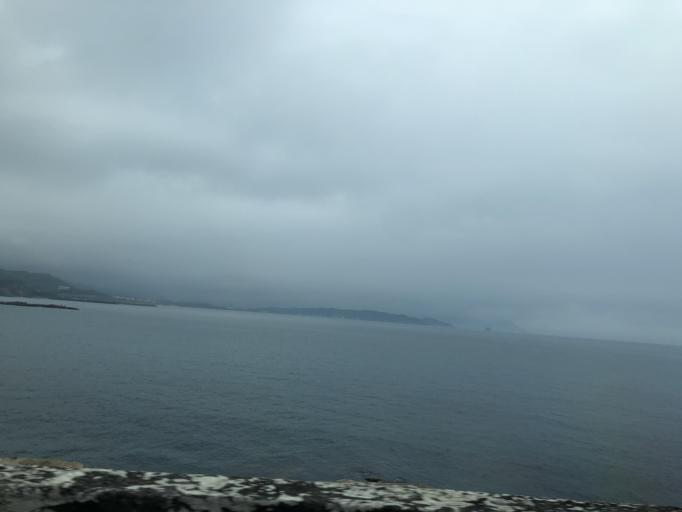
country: TW
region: Taiwan
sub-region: Keelung
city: Keelung
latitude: 25.2054
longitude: 121.6831
